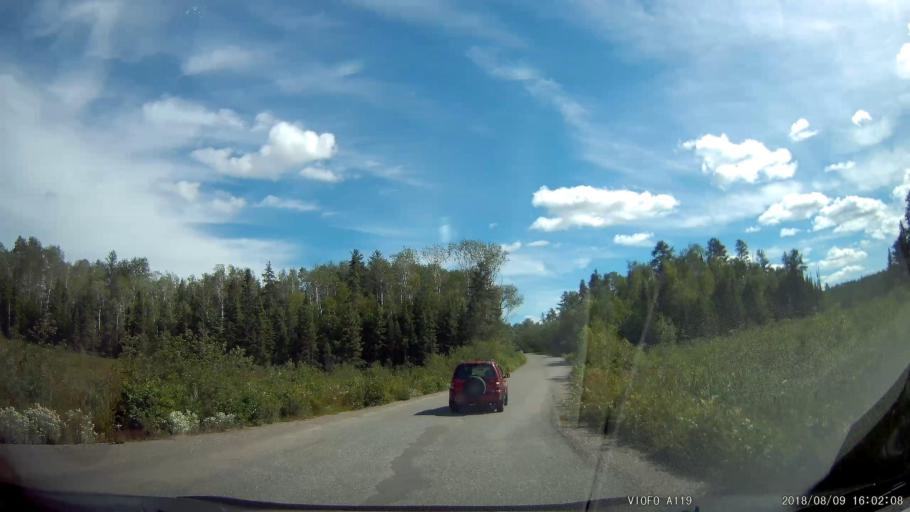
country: CA
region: Ontario
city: Rayside-Balfour
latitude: 46.6157
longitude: -81.4660
